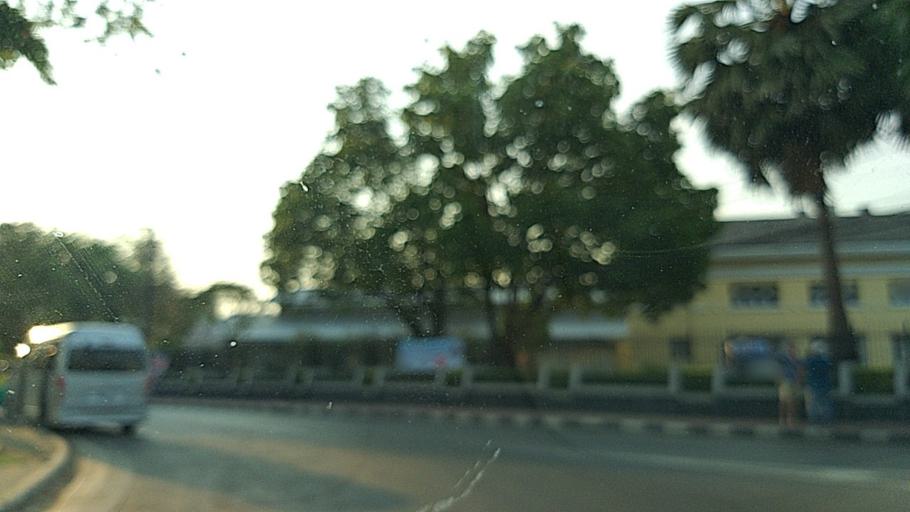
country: TH
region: Bangkok
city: Phra Nakhon
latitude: 13.7584
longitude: 100.4948
